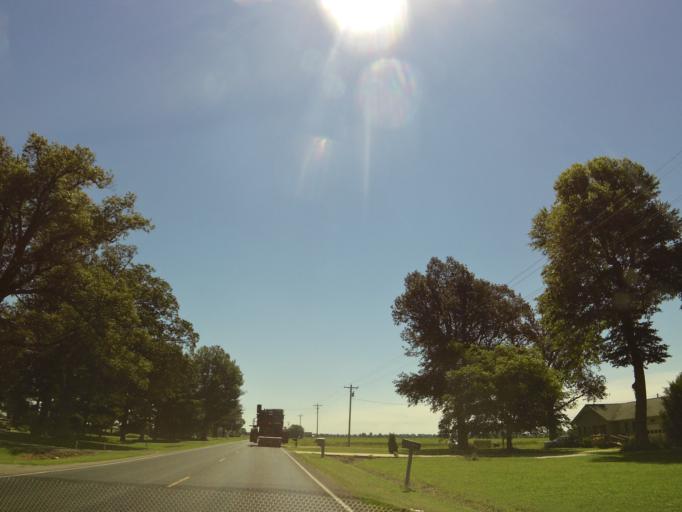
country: US
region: Missouri
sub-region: New Madrid County
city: Portageville
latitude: 36.5536
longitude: -89.7821
